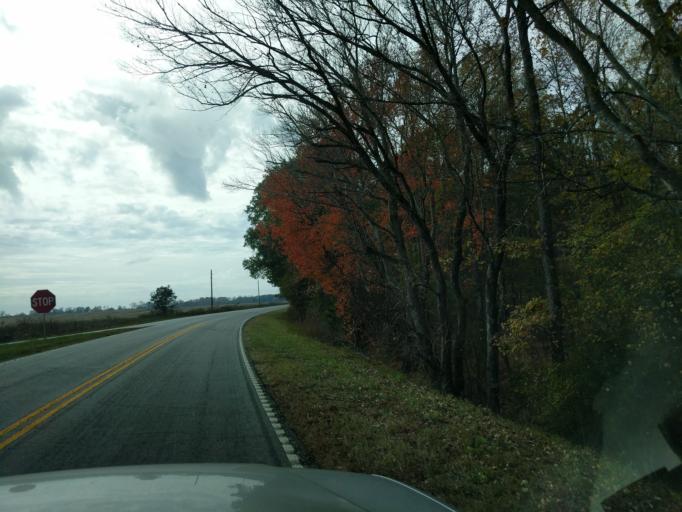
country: US
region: South Carolina
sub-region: Laurens County
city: Joanna
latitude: 34.3972
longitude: -81.8518
